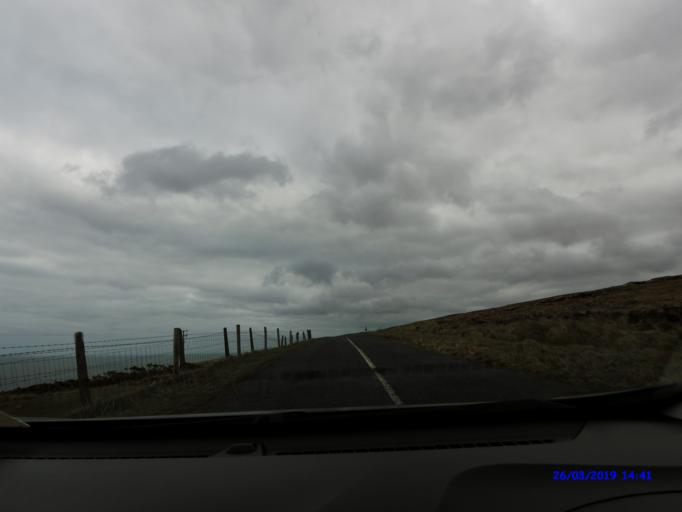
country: IE
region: Connaught
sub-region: Maigh Eo
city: Crossmolina
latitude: 54.3090
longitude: -9.4673
